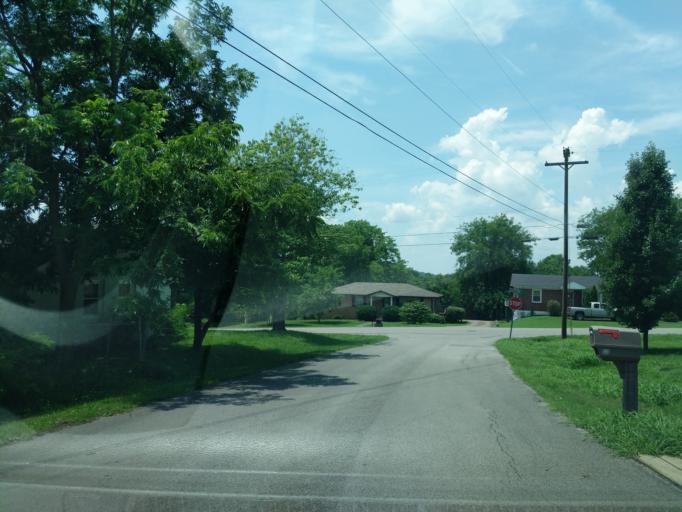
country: US
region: Tennessee
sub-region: Davidson County
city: Lakewood
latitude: 36.2352
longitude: -86.6320
